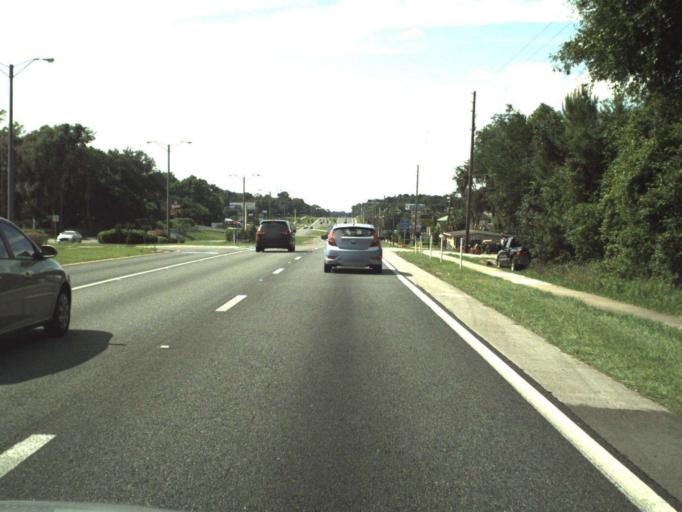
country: US
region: Florida
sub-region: Marion County
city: Belleview
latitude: 29.0684
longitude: -82.0697
